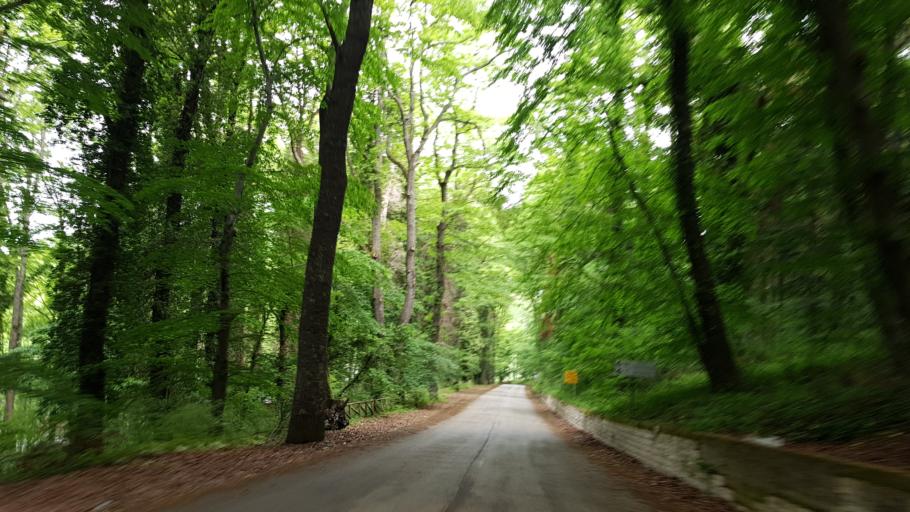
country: IT
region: Basilicate
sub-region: Provincia di Potenza
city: Rionero in Vulture
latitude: 40.9283
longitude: 15.6127
